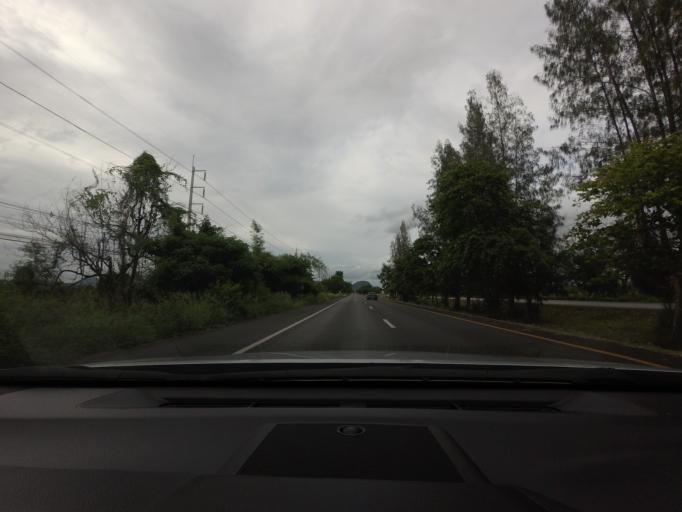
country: TH
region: Prachuap Khiri Khan
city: Hua Hin
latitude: 12.6590
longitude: 99.8746
